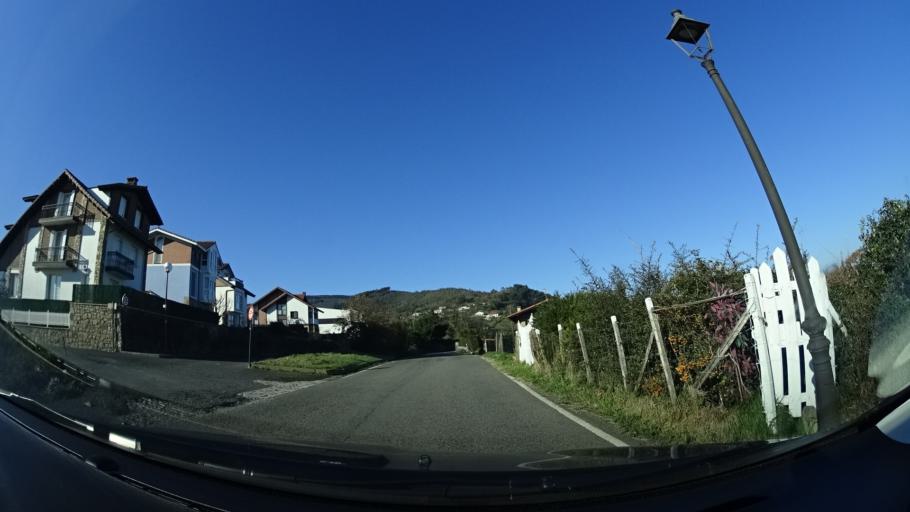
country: ES
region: Basque Country
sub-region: Bizkaia
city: Bermeo
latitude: 43.4228
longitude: -2.7307
